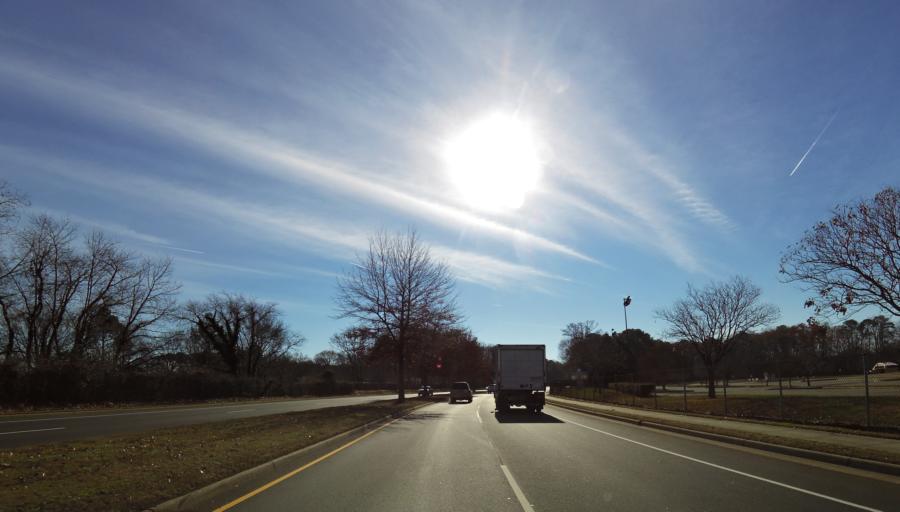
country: US
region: Virginia
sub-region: City of Hampton
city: Hampton
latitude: 37.0243
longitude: -76.3875
